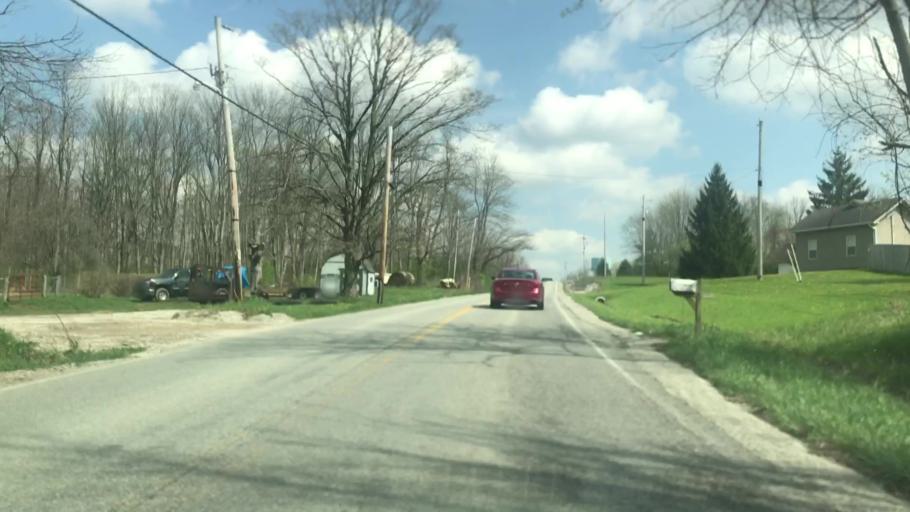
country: US
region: Indiana
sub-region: Johnson County
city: Waterloo
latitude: 39.5516
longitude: -86.2100
